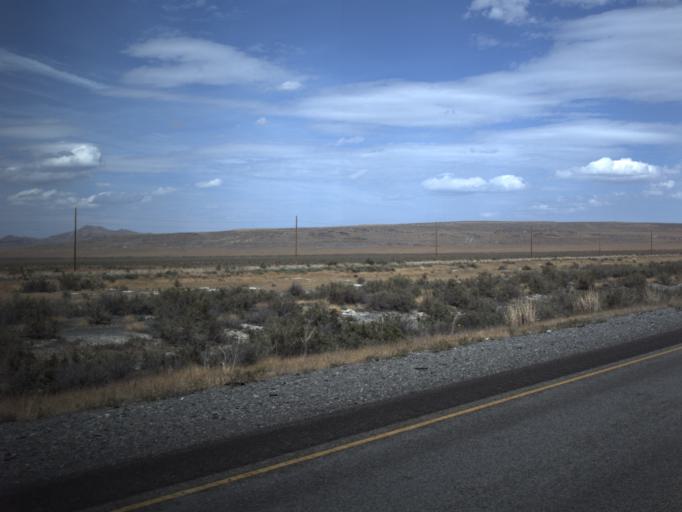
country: US
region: Utah
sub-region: Tooele County
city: Grantsville
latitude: 40.7436
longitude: -113.0697
